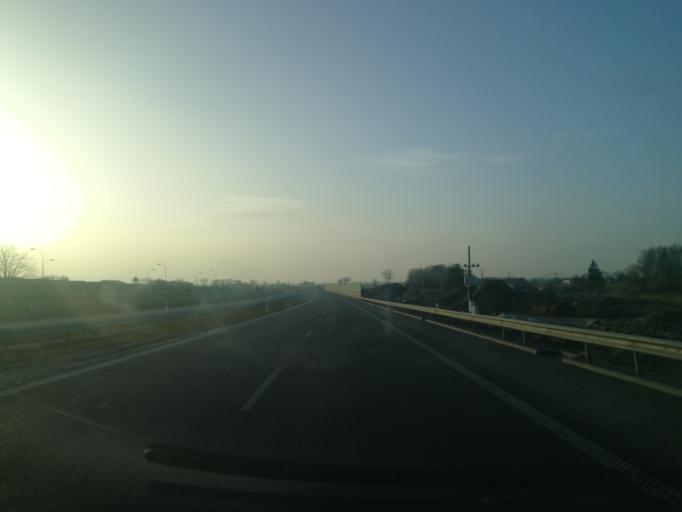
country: PL
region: Pomeranian Voivodeship
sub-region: Powiat nowodworski
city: Ostaszewo
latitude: 54.2594
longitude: 18.9323
